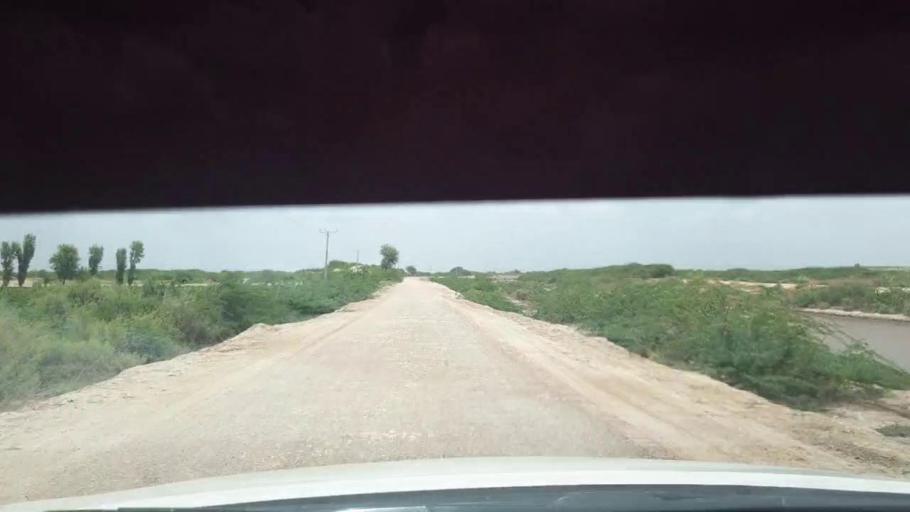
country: PK
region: Sindh
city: Kadhan
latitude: 24.5213
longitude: 69.1220
